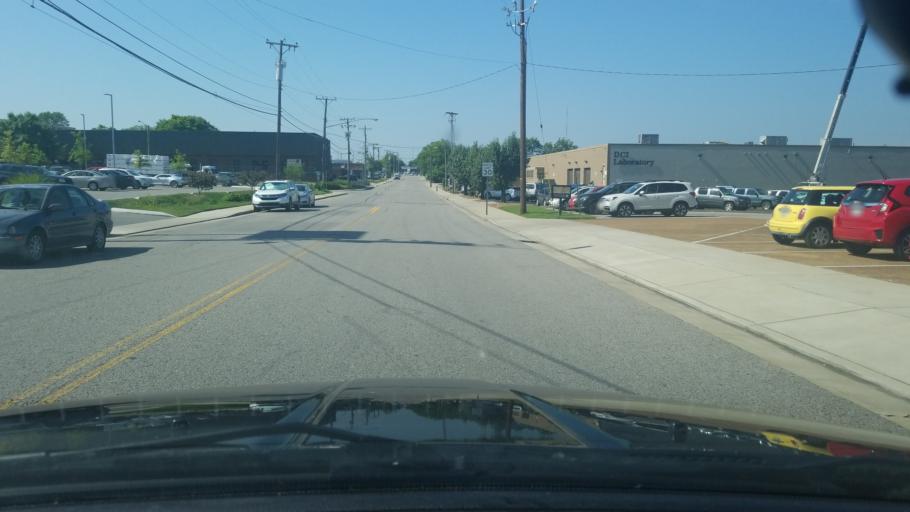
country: US
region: Tennessee
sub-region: Davidson County
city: Oak Hill
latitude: 36.1106
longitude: -86.7536
